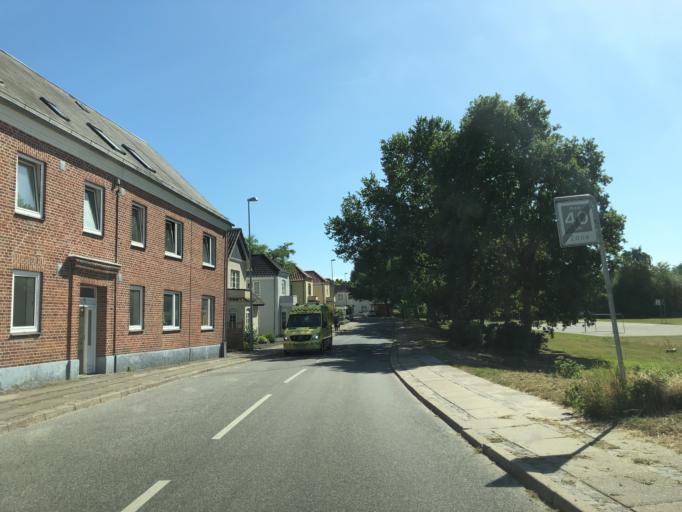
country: DK
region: North Denmark
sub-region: Mariagerfjord Kommune
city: Hobro
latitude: 56.6352
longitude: 9.7926
